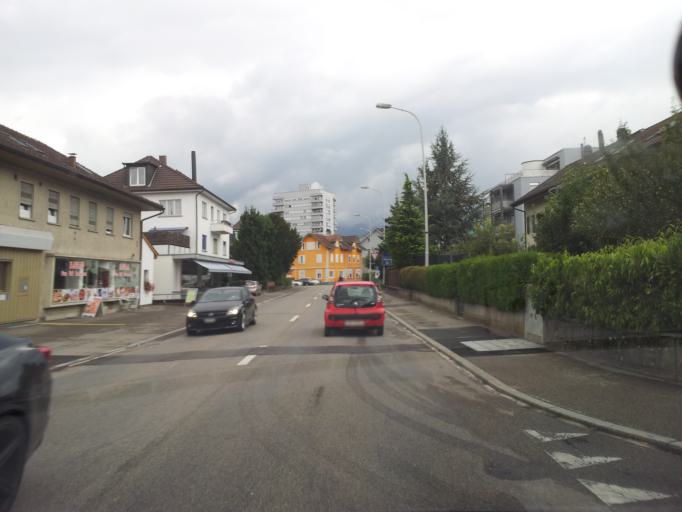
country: CH
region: Solothurn
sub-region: Bezirk Wasseramt
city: Derendingen
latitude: 47.1983
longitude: 7.5832
